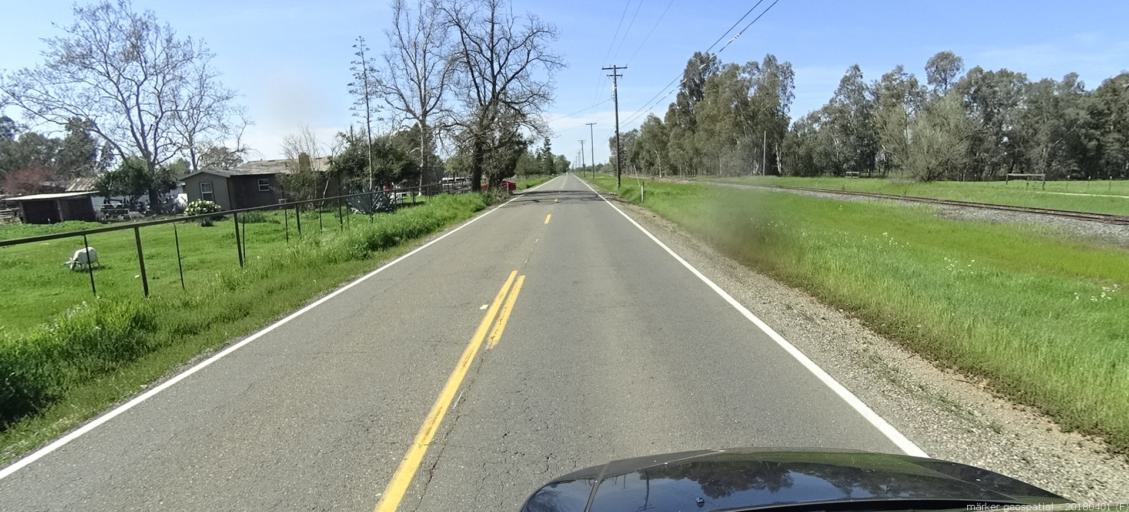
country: US
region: California
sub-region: Sacramento County
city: Wilton
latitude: 38.4024
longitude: -121.2588
